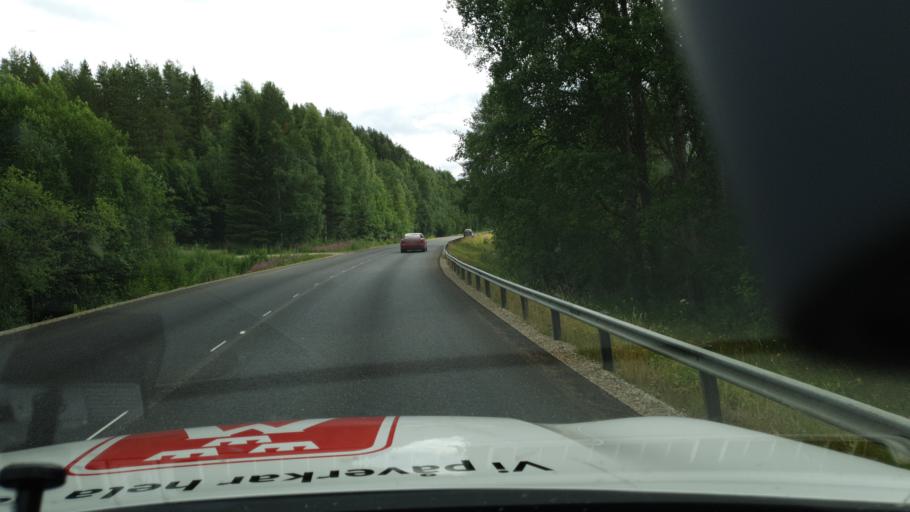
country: SE
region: Vaesterbotten
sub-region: Vindelns Kommun
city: Vindeln
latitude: 64.3113
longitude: 19.6069
